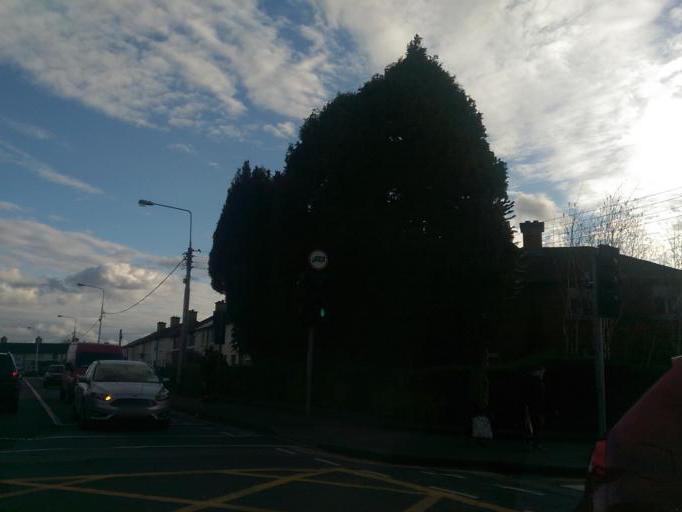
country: IE
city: Greenhills
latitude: 53.3394
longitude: -6.3077
